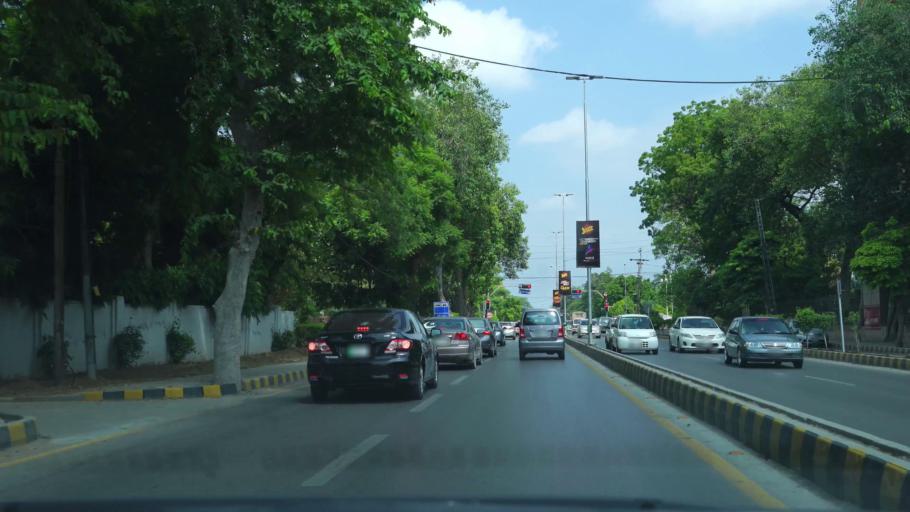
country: PK
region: Punjab
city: Lahore
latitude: 31.5282
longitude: 74.3767
